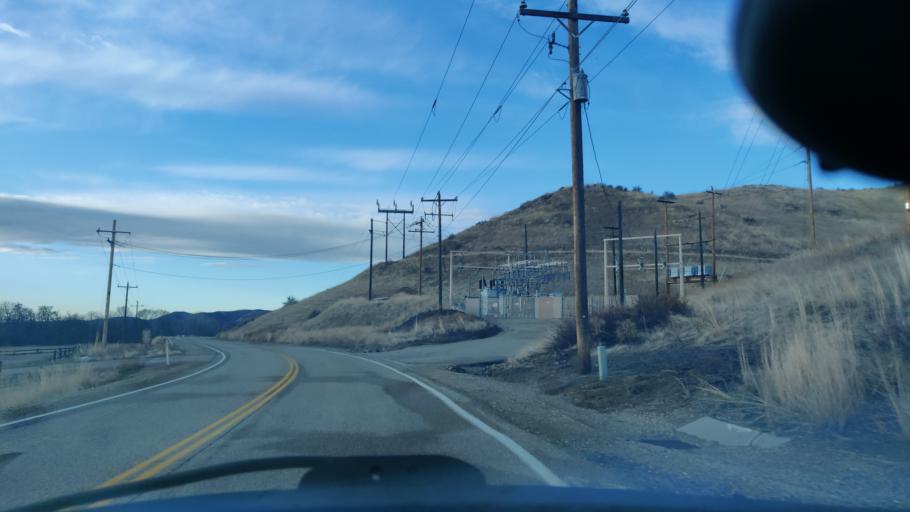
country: US
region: Idaho
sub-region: Ada County
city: Garden City
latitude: 43.7253
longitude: -116.2473
